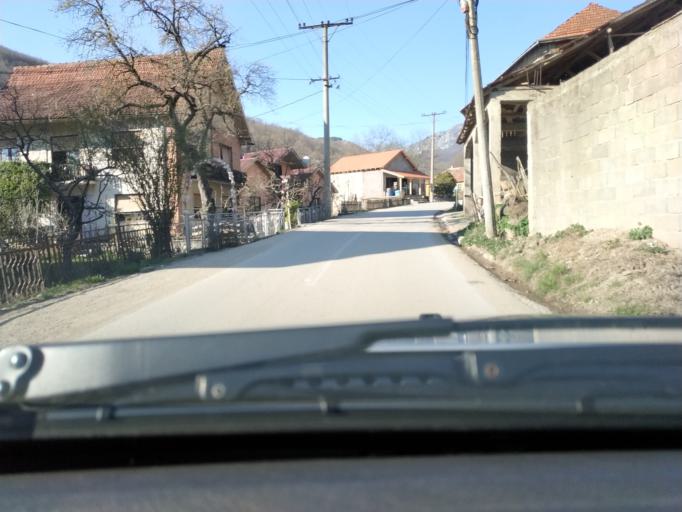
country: RS
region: Central Serbia
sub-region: Zajecarski Okrug
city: Soko Banja
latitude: 43.5539
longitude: 21.8159
